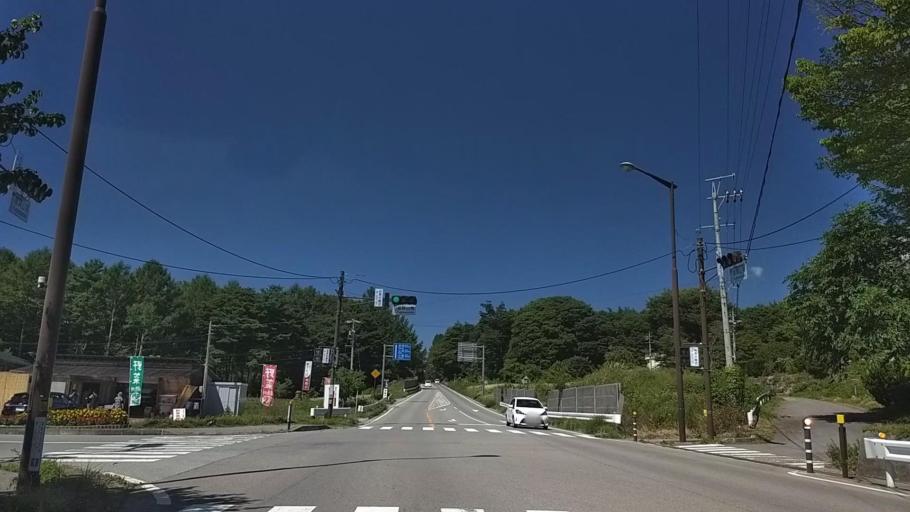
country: JP
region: Nagano
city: Komoro
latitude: 36.3392
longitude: 138.5015
